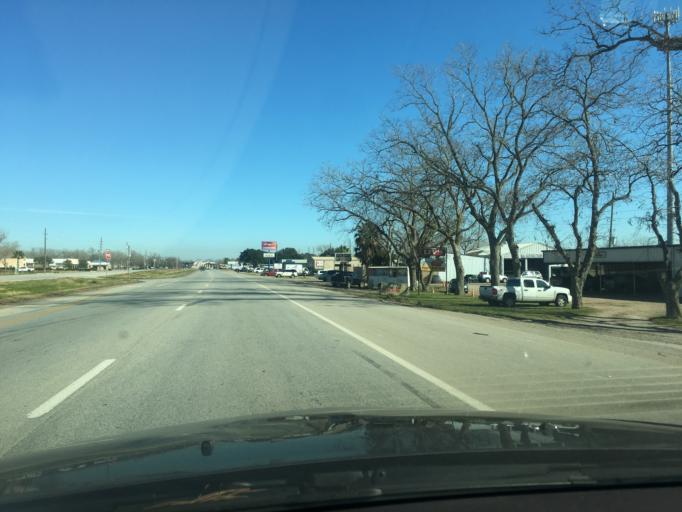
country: US
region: Texas
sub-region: Fort Bend County
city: Richmond
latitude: 29.5865
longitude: -95.7515
